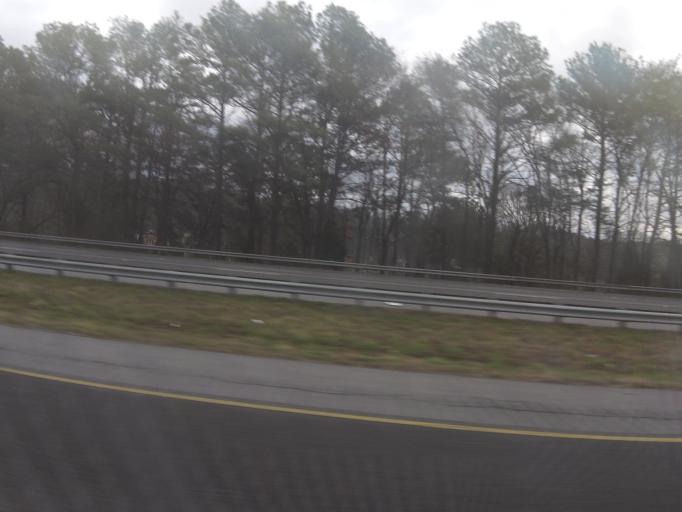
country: US
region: Georgia
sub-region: Whitfield County
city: Dalton
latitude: 34.7699
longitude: -85.0015
